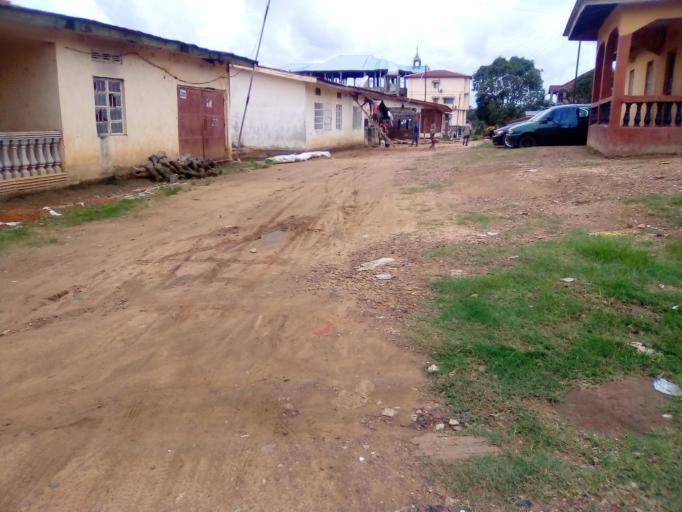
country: SL
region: Southern Province
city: Bo
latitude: 7.9466
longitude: -11.7274
